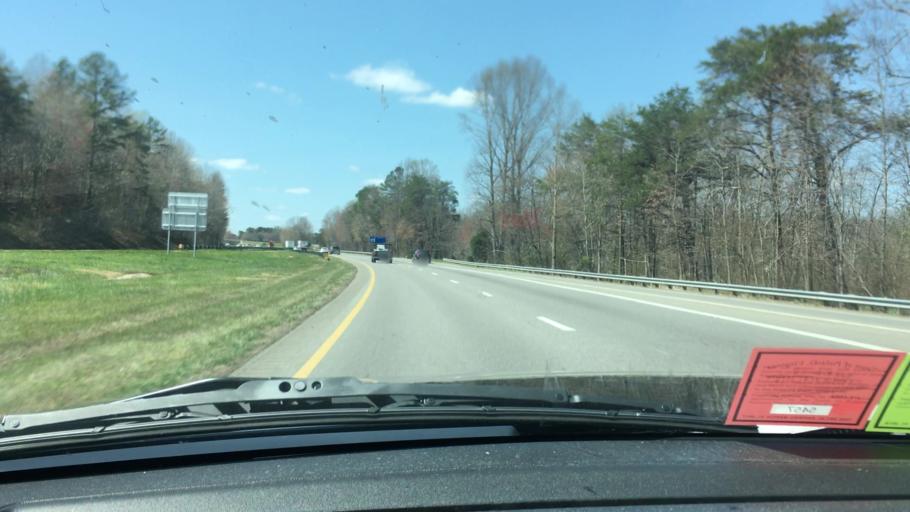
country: US
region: North Carolina
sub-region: Surry County
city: Pilot Mountain
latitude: 36.4023
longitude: -80.4928
